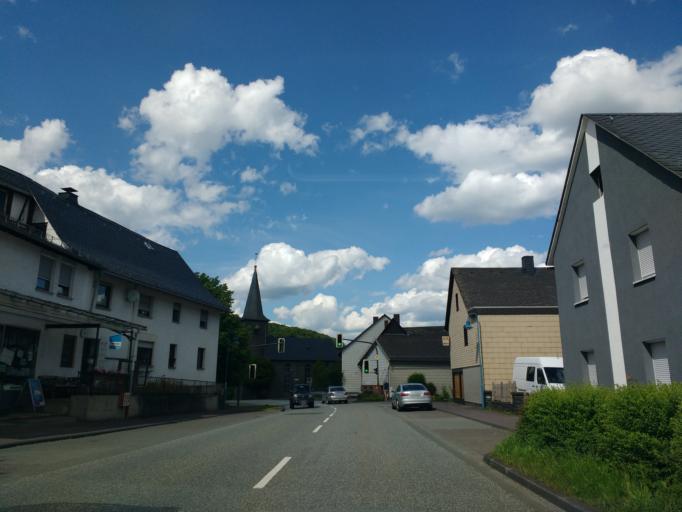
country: DE
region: Hesse
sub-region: Regierungsbezirk Giessen
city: Breidenbach
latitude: 50.8570
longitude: 8.4149
